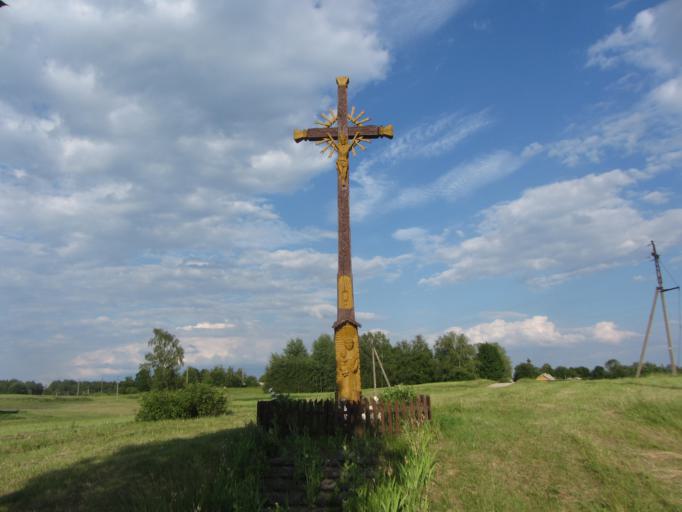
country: LT
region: Alytaus apskritis
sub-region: Alytaus rajonas
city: Daugai
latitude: 54.4497
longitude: 24.2090
